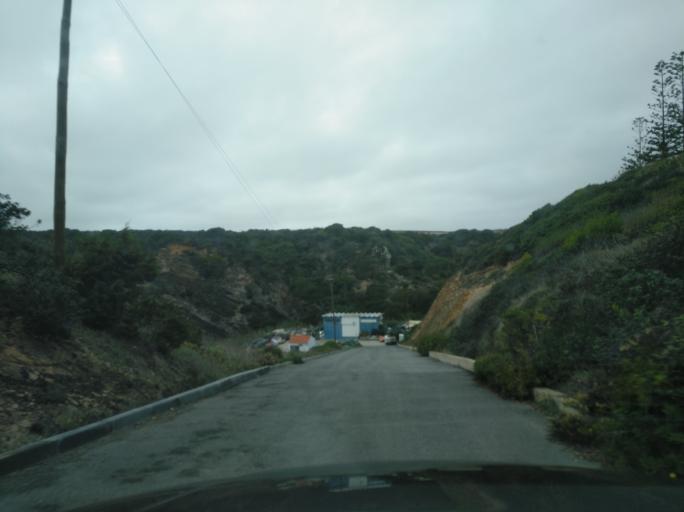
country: PT
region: Beja
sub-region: Odemira
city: Sao Teotonio
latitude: 37.5516
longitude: -8.7915
